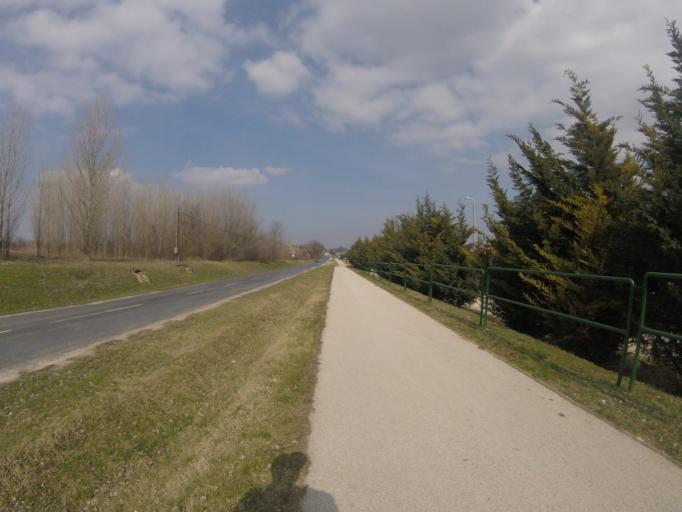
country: HU
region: Komarom-Esztergom
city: Nyergesujfalu
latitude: 47.7528
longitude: 18.5543
